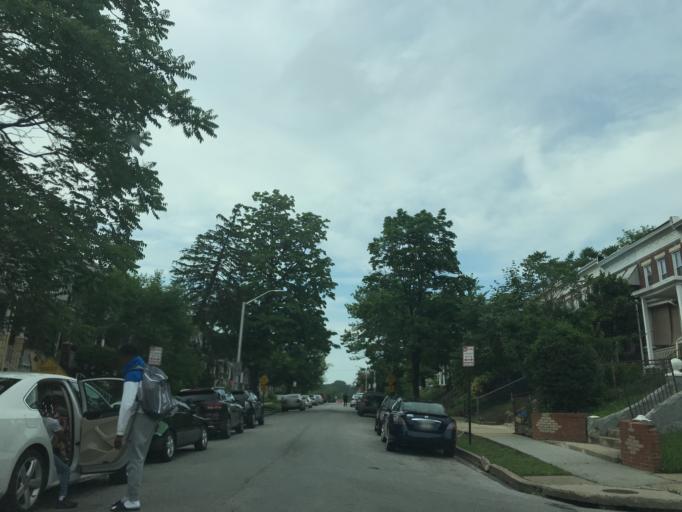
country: US
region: Maryland
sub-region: City of Baltimore
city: Baltimore
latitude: 39.3070
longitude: -76.6621
